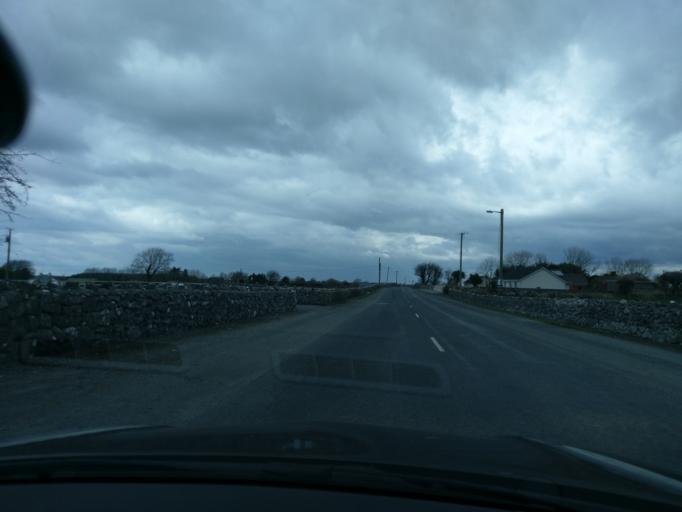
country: IE
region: Connaught
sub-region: County Galway
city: Athenry
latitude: 53.4162
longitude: -8.6357
